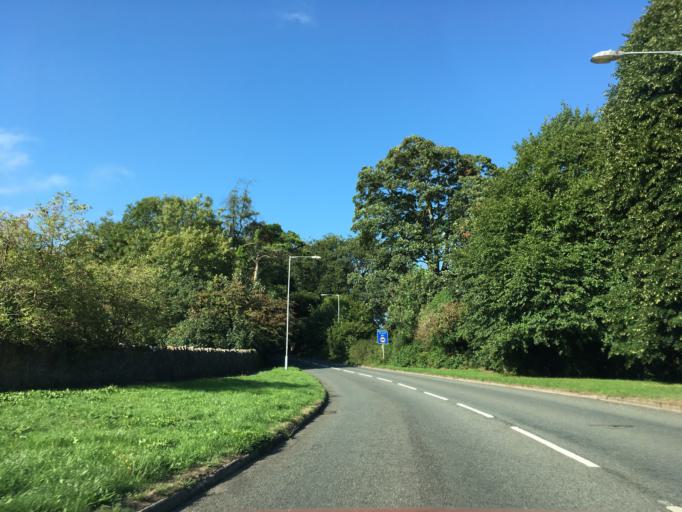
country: GB
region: England
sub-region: Somerset
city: Mendip
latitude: 51.2130
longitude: -2.6213
